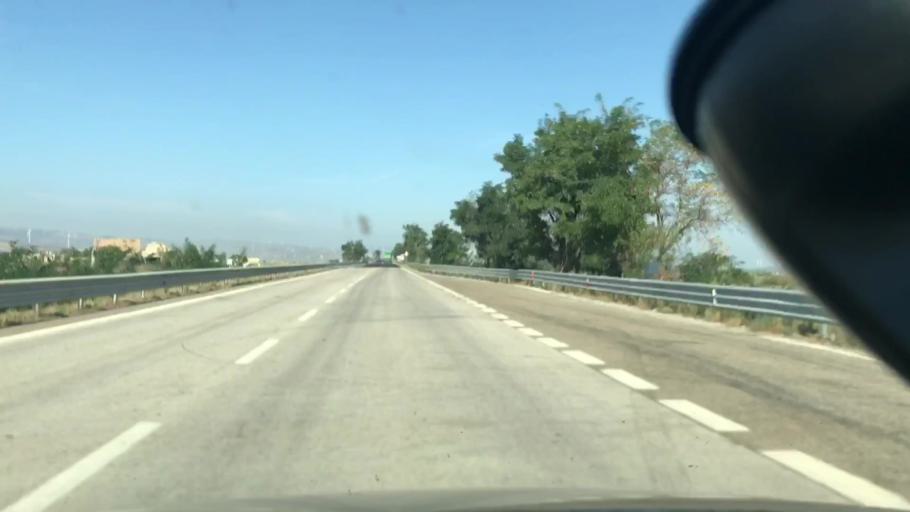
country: IT
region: Basilicate
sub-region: Provincia di Potenza
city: Zona 179
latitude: 41.0732
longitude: 15.6485
